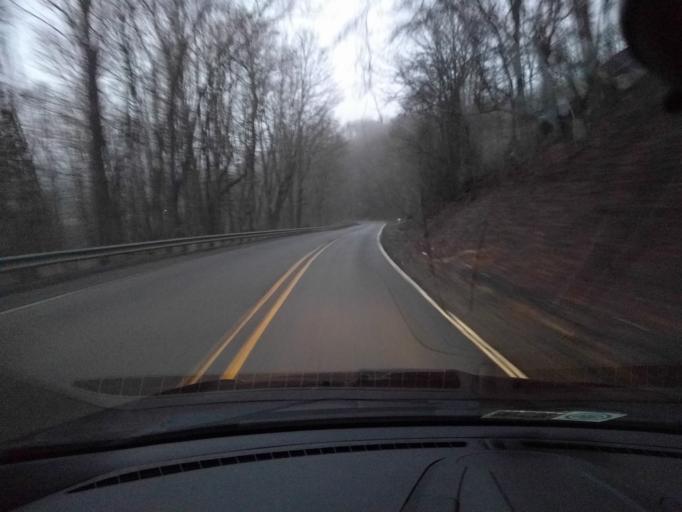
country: US
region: West Virginia
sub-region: Greenbrier County
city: Rainelle
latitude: 37.9767
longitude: -80.8212
